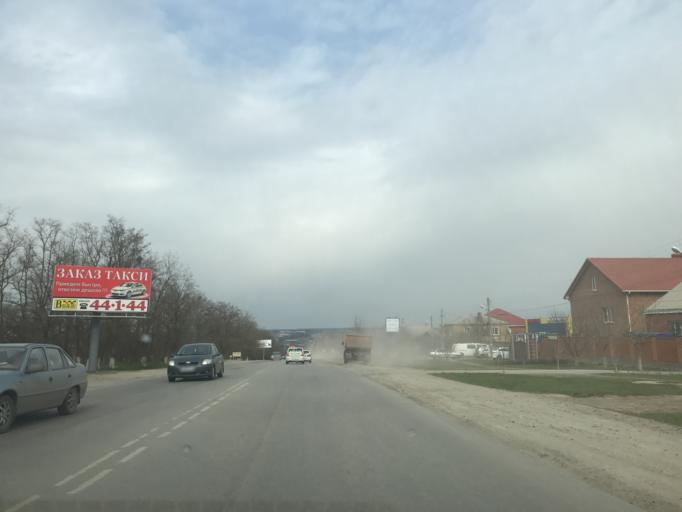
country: RU
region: Rostov
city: Aksay
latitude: 47.2839
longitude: 39.9030
